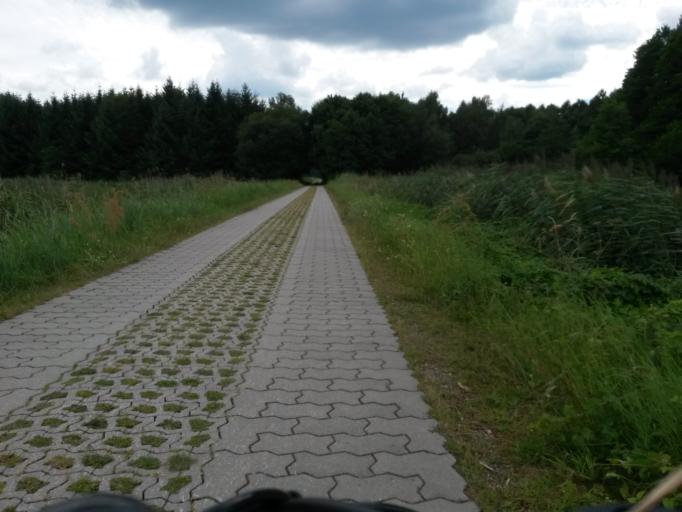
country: DE
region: Brandenburg
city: Angermunde
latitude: 53.0448
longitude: 13.9425
